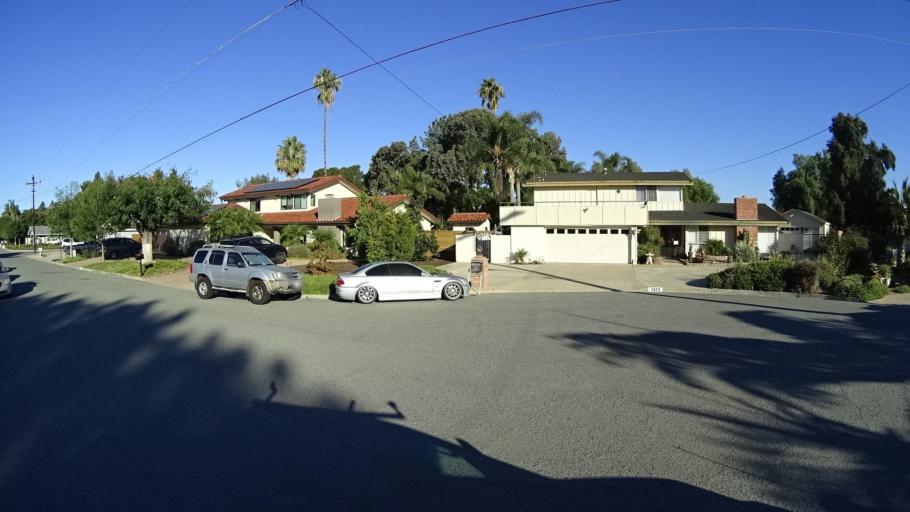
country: US
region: California
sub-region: San Diego County
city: Bonita
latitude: 32.6740
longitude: -117.0262
